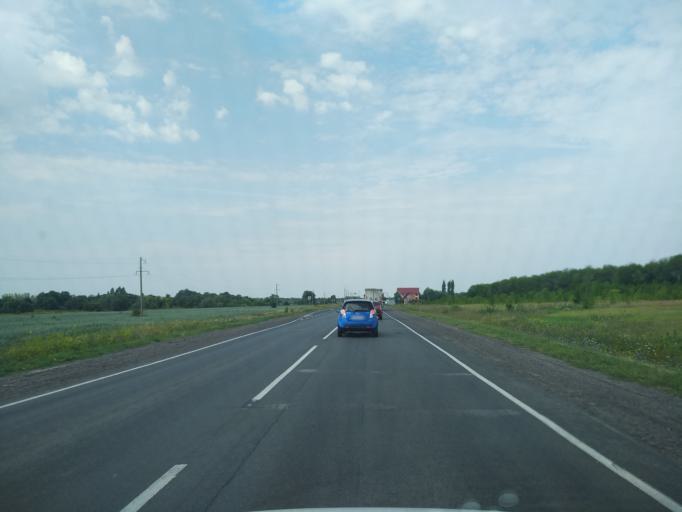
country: RU
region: Voronezj
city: Orlovo
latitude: 51.6797
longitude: 39.6558
